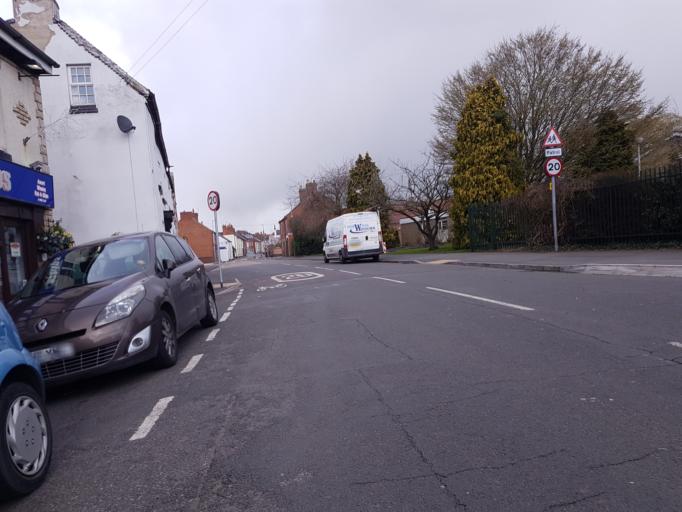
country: GB
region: England
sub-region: Leicestershire
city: Earl Shilton
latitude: 52.5650
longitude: -1.3487
